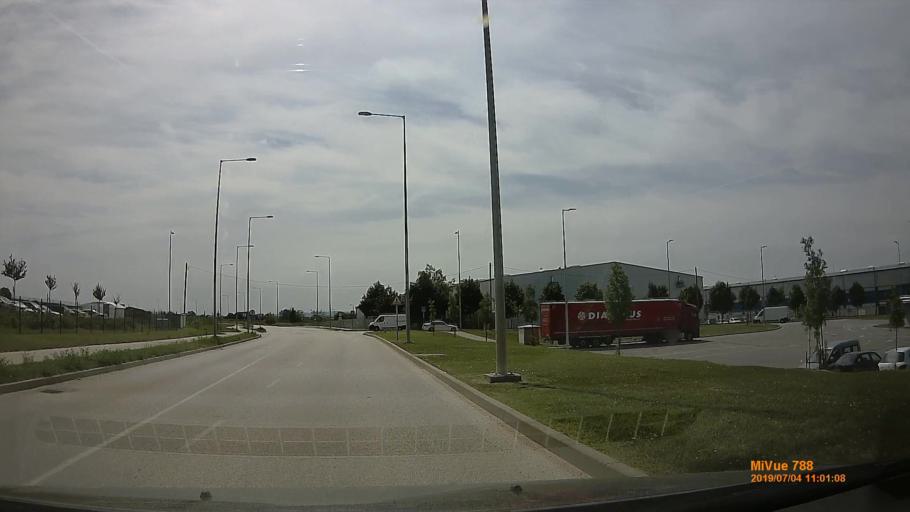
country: HU
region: Komarom-Esztergom
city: Tata
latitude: 47.6314
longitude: 18.2953
